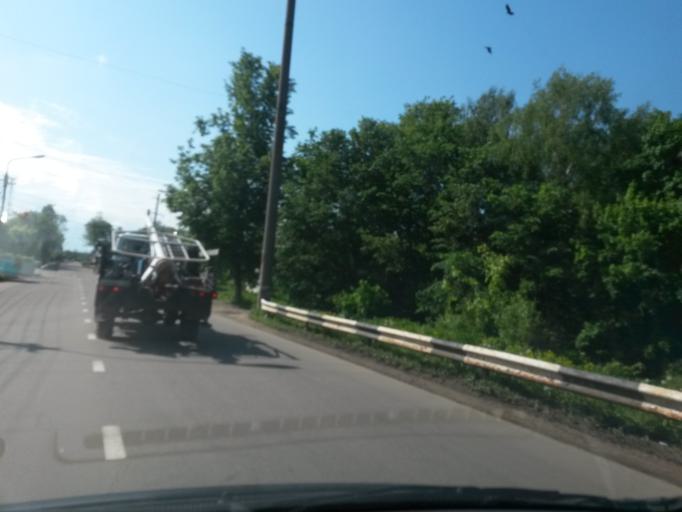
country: RU
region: Jaroslavl
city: Gavrilov-Yam
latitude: 57.3061
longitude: 39.8527
